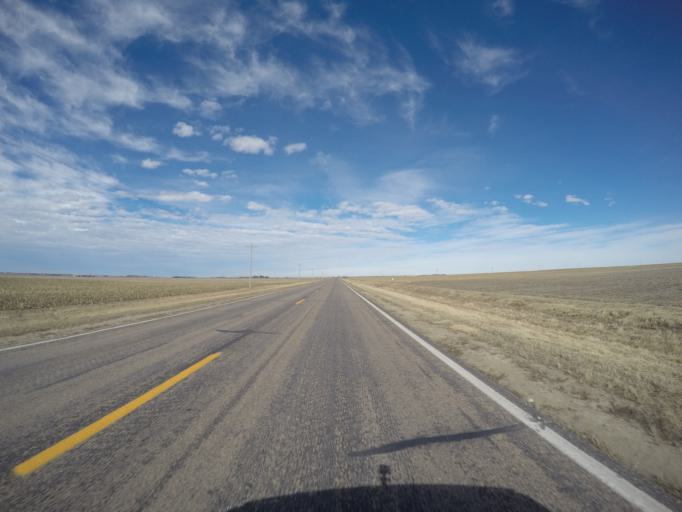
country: US
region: Nebraska
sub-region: Franklin County
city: Franklin
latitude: 40.2309
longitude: -98.9524
